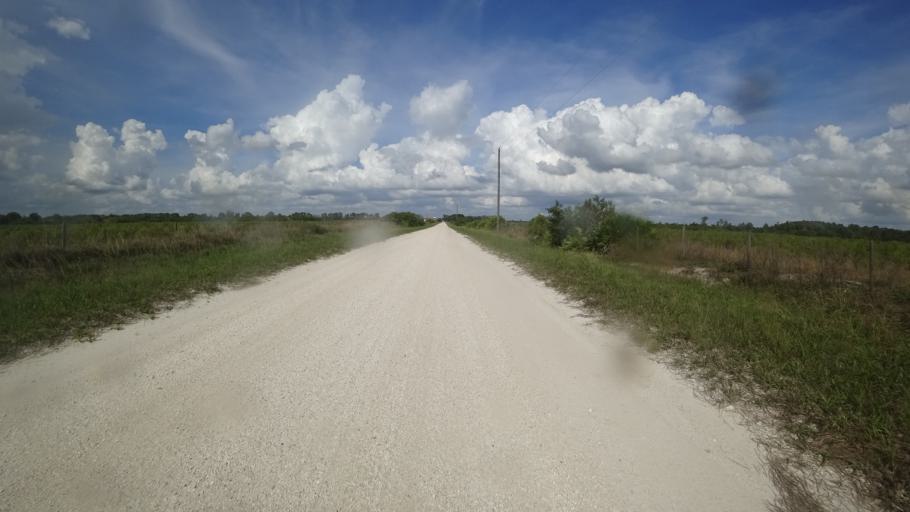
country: US
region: Florida
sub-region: Hillsborough County
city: Wimauma
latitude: 27.5778
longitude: -82.1740
